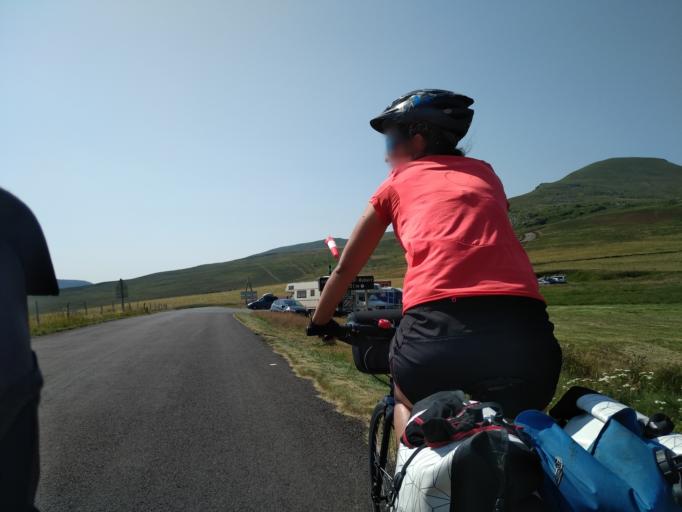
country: FR
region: Auvergne
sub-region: Departement du Puy-de-Dome
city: Mont-Dore
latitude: 45.5626
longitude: 2.8382
